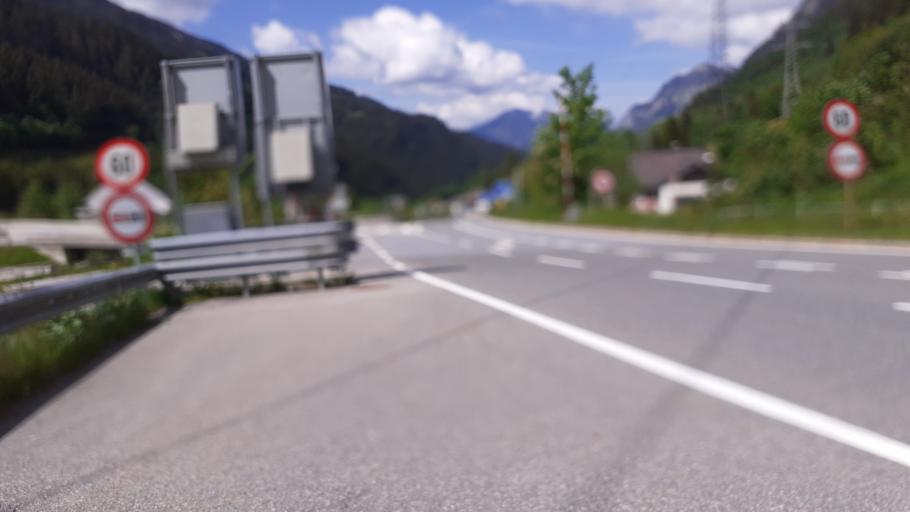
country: AT
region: Vorarlberg
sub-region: Politischer Bezirk Bludenz
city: Klosterle
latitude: 47.1319
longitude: 10.1159
